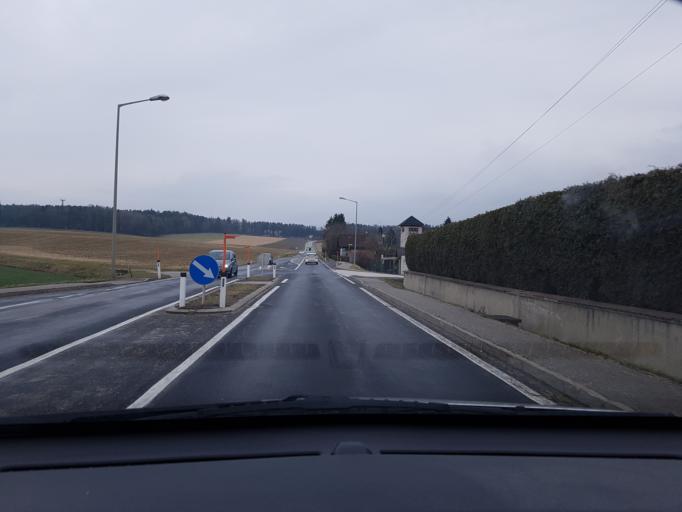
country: AT
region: Upper Austria
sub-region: Steyr Stadt
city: Steyr
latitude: 48.0704
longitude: 14.3830
